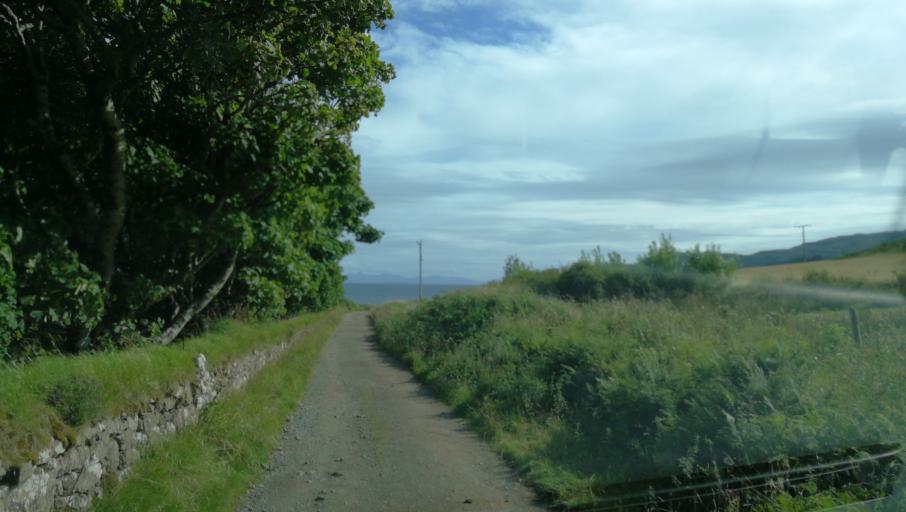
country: GB
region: Scotland
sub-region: Highland
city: Isle of Skye
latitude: 57.3935
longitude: -6.5657
